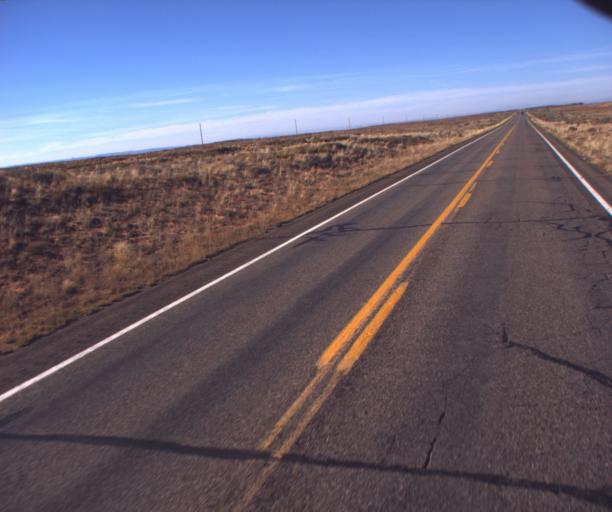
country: US
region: Arizona
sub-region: Coconino County
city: Kaibito
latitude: 36.6983
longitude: -111.2639
